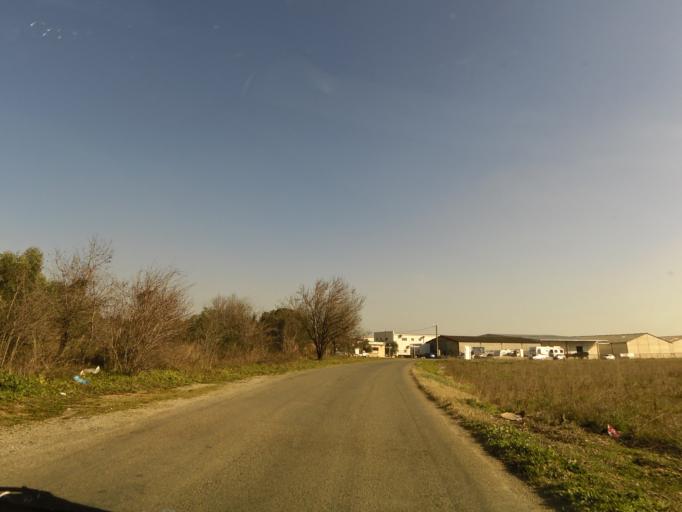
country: FR
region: Languedoc-Roussillon
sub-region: Departement du Gard
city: Codognan
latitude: 43.7284
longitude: 4.2115
